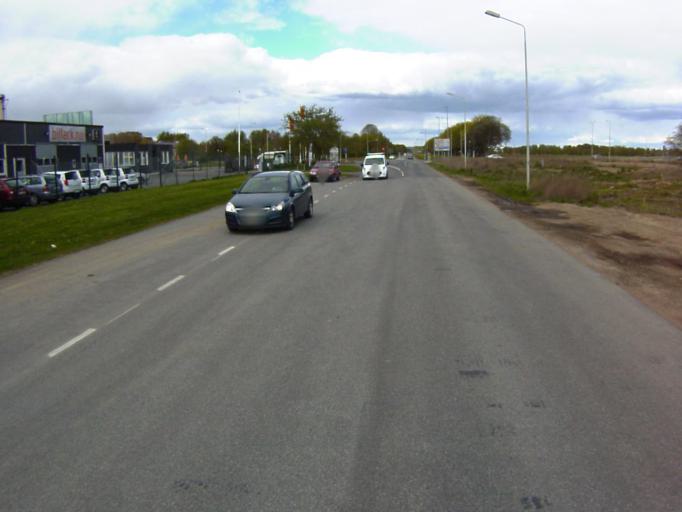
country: SE
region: Skane
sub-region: Kristianstads Kommun
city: Kristianstad
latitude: 56.0284
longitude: 14.1846
